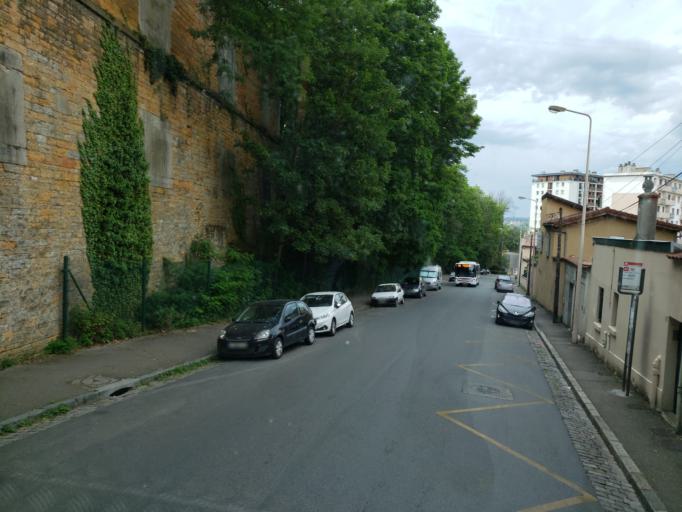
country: FR
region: Rhone-Alpes
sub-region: Departement du Rhone
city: Tassin-la-Demi-Lune
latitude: 45.7659
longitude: 4.8100
